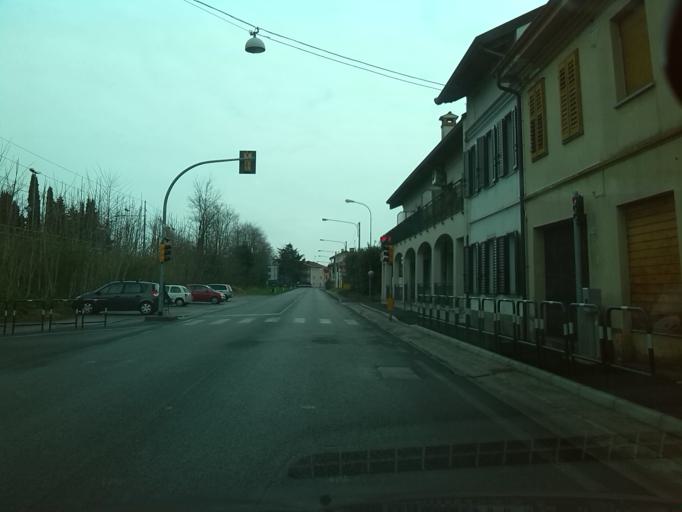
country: IT
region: Friuli Venezia Giulia
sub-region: Provincia di Gorizia
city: Capriva del Friuli
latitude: 45.9390
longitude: 13.5140
